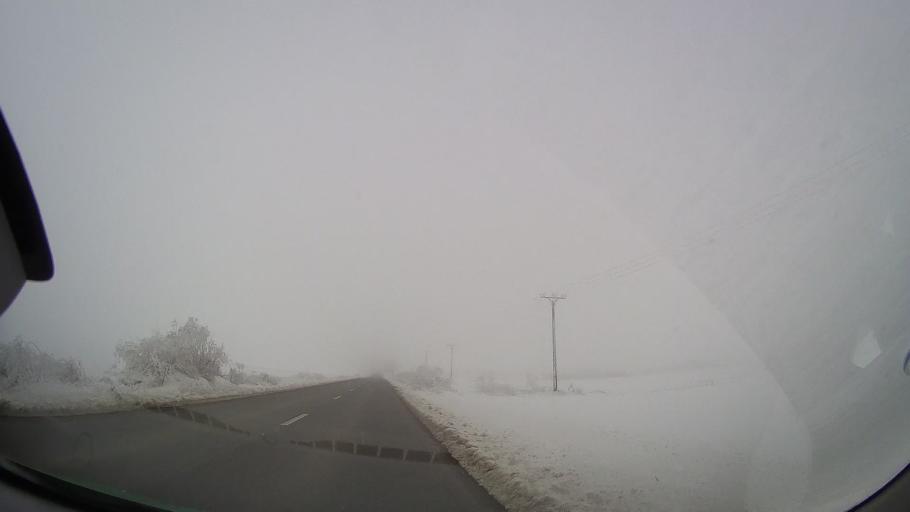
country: RO
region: Iasi
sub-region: Comuna Mogosesti-Siret
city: Mogosesti-Siret
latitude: 47.1436
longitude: 26.7792
